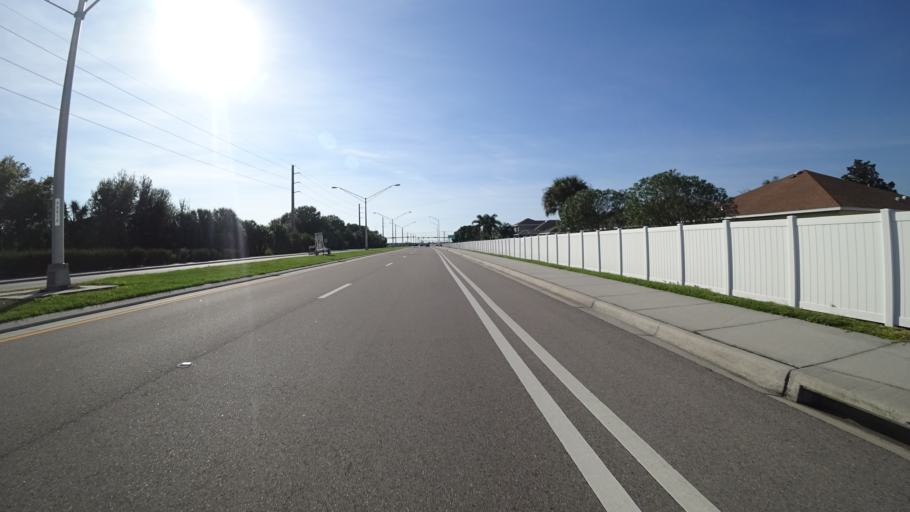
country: US
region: Florida
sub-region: Manatee County
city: Samoset
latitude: 27.4616
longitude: -82.5231
